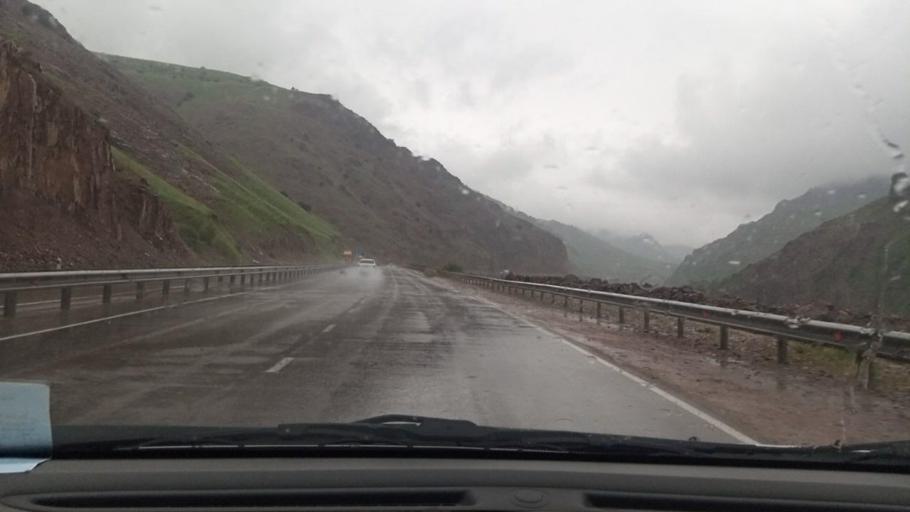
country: UZ
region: Toshkent
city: Angren
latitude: 41.1103
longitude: 70.3372
